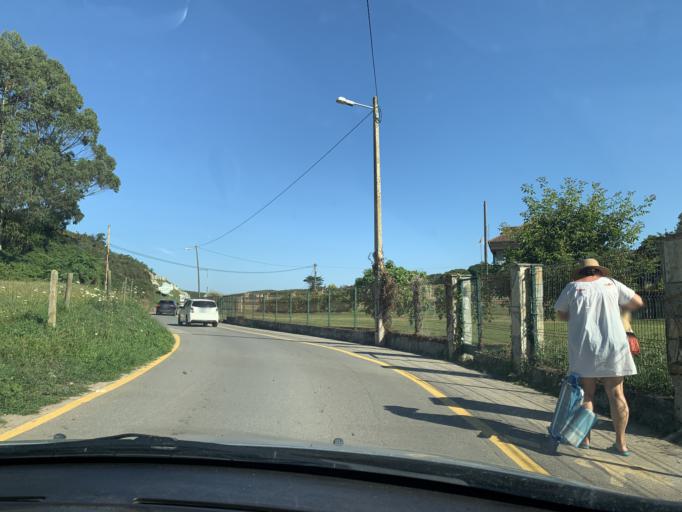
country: ES
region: Asturias
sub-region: Province of Asturias
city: Llanes
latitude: 43.4280
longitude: -4.7824
